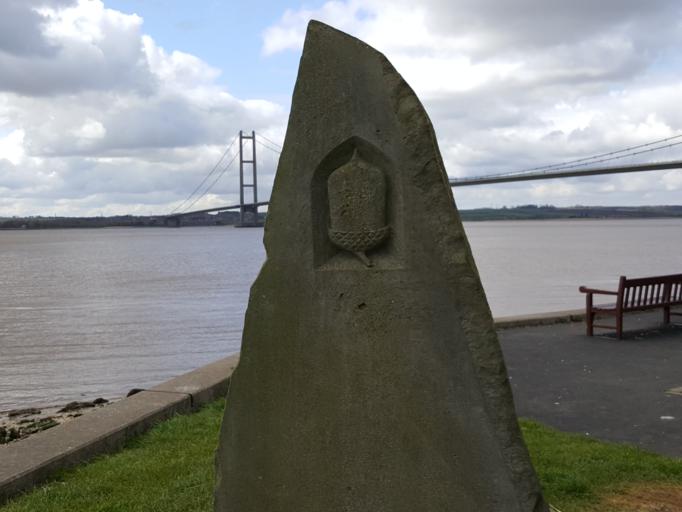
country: GB
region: England
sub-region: East Riding of Yorkshire
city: Hessle
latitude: 53.7147
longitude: -0.4433
